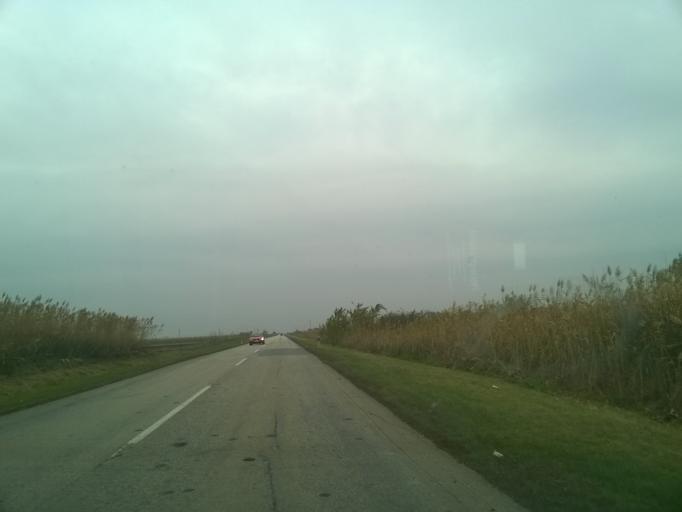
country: RS
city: Crepaja
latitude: 44.9531
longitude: 20.6621
